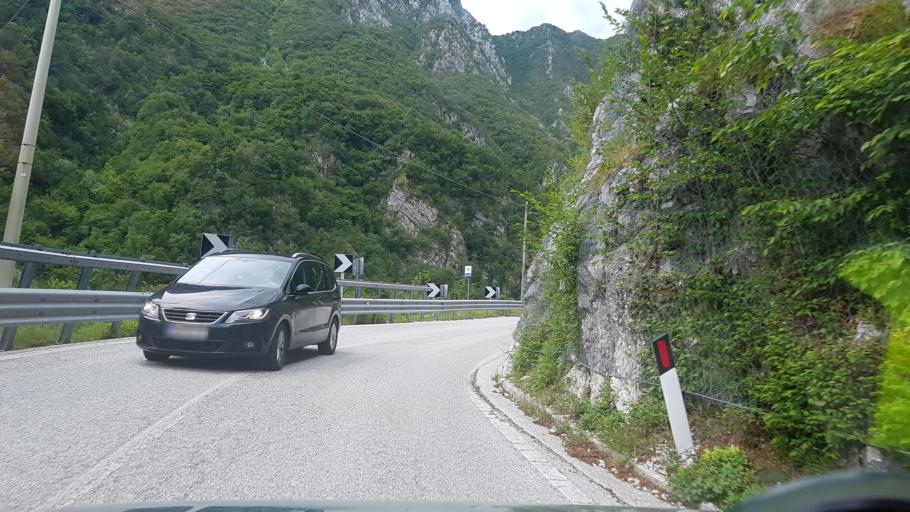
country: IT
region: Friuli Venezia Giulia
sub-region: Provincia di Udine
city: Lusevera
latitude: 46.2945
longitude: 13.2700
